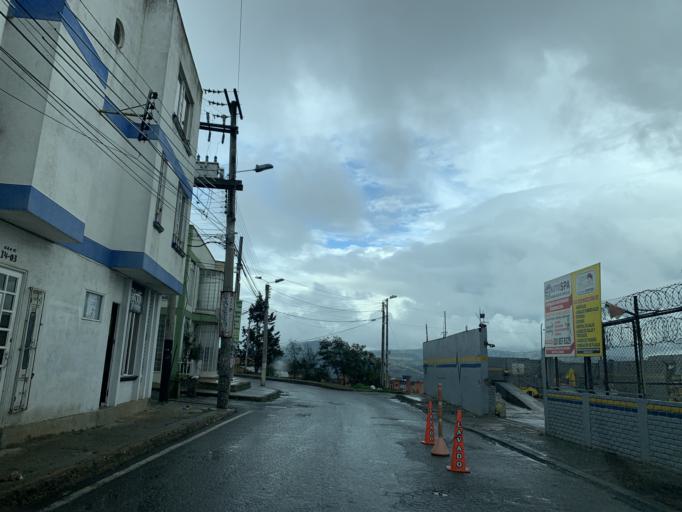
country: CO
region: Boyaca
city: Tunja
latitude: 5.5282
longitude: -73.3663
